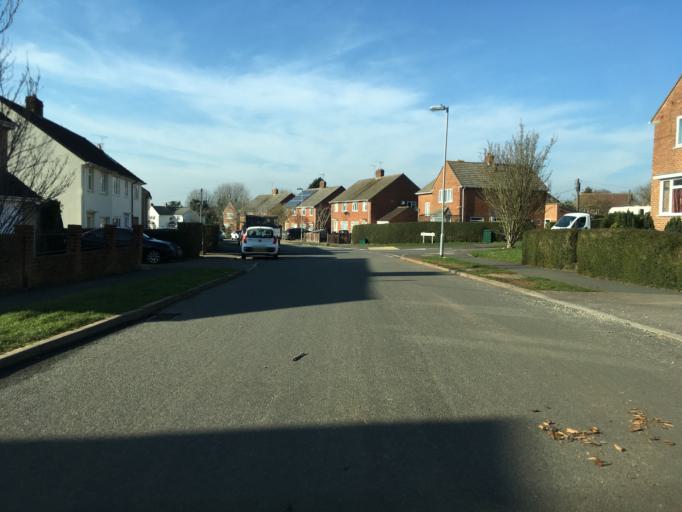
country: GB
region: England
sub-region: South Gloucestershire
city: Chipping Sodbury
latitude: 51.5440
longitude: -2.4027
